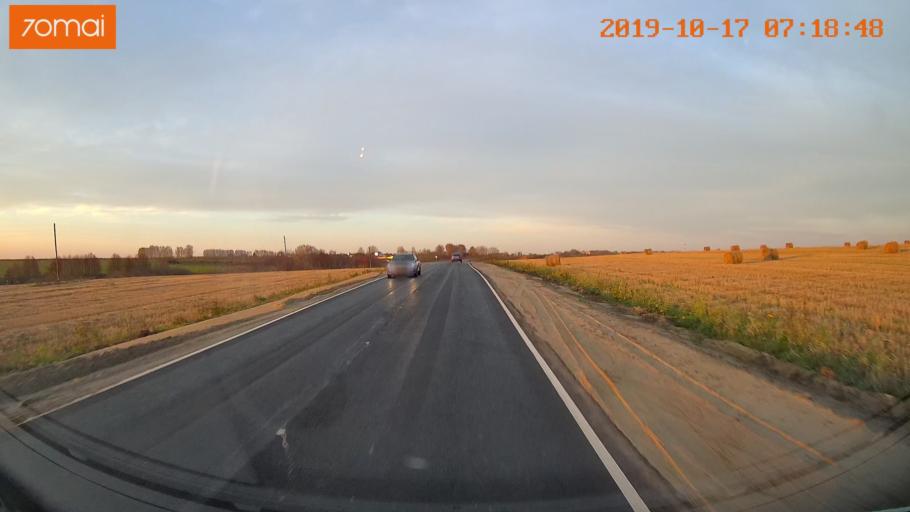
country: RU
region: Ivanovo
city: Gavrilov Posad
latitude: 56.3501
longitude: 40.2118
